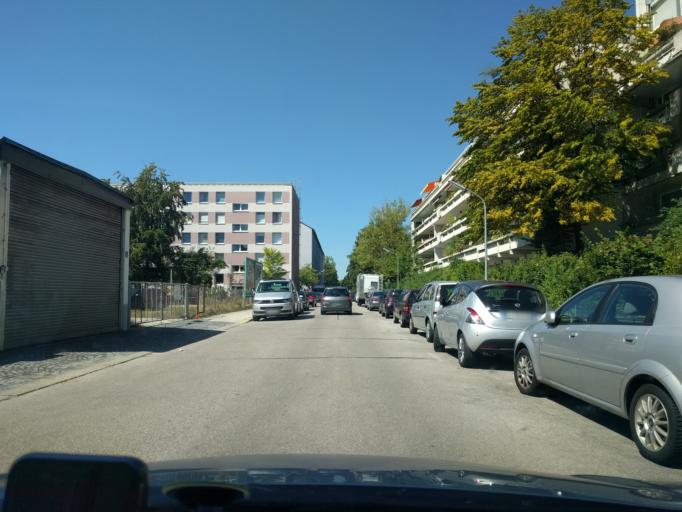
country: DE
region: Bavaria
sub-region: Upper Bavaria
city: Munich
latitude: 48.1359
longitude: 11.5186
